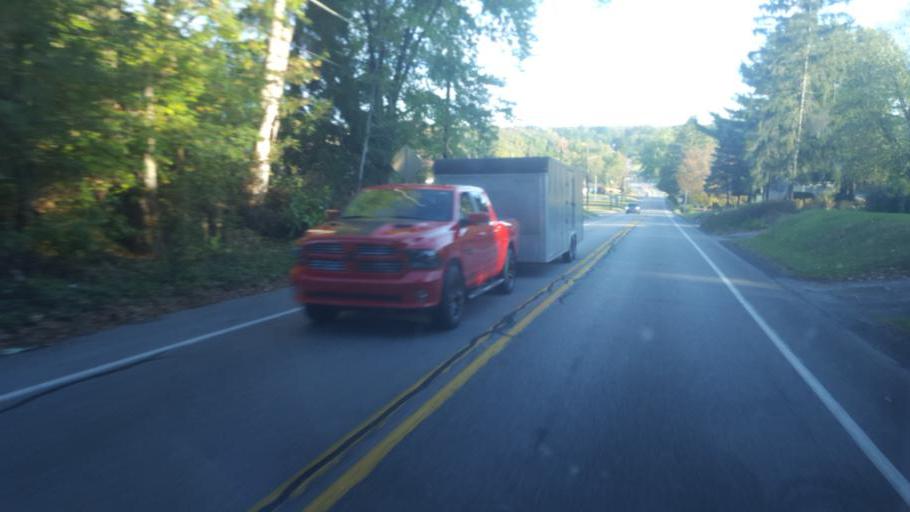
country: US
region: Pennsylvania
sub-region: Mercer County
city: Mercer
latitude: 41.2313
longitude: -80.2394
